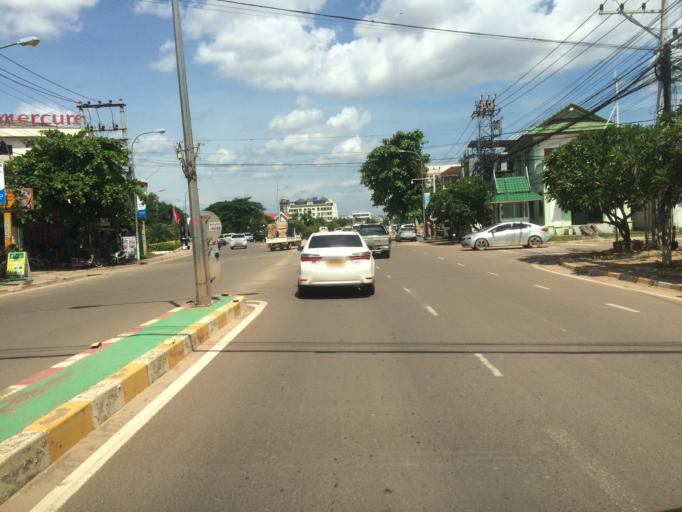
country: LA
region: Vientiane
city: Vientiane
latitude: 17.9685
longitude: 102.5932
